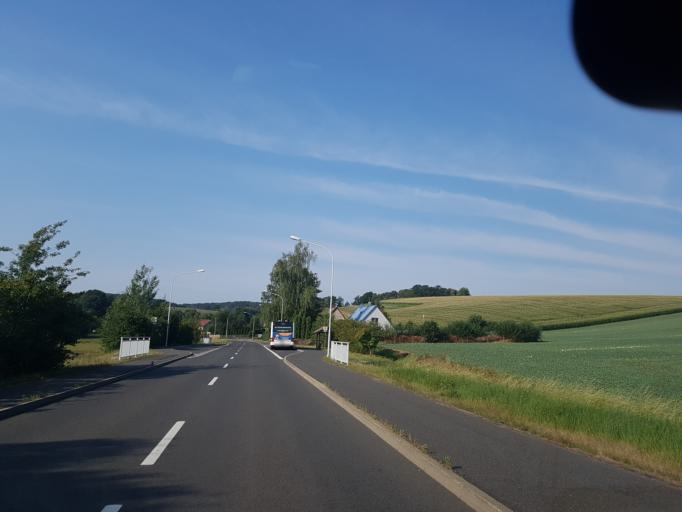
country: DE
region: Saxony
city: Waldheim
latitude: 51.0864
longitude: 13.0664
